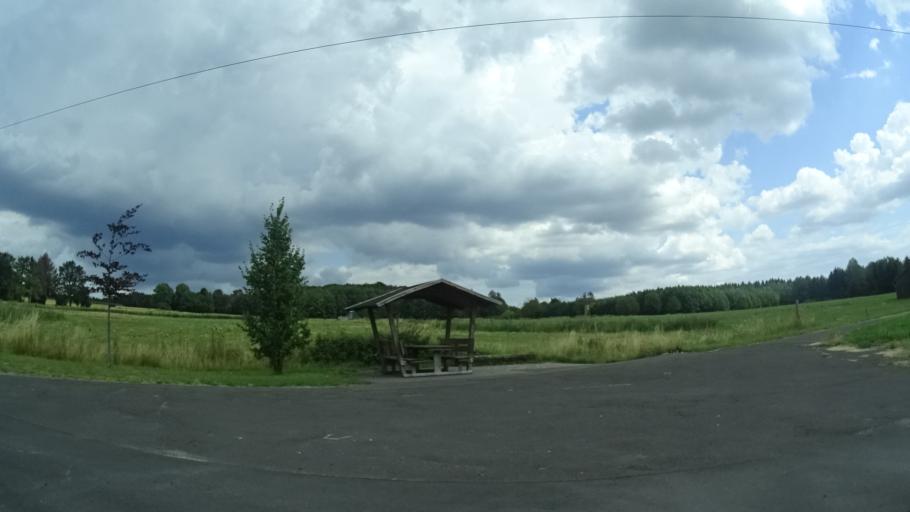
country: DE
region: Hesse
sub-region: Regierungsbezirk Giessen
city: Grebenhain
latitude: 50.4428
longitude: 9.2825
